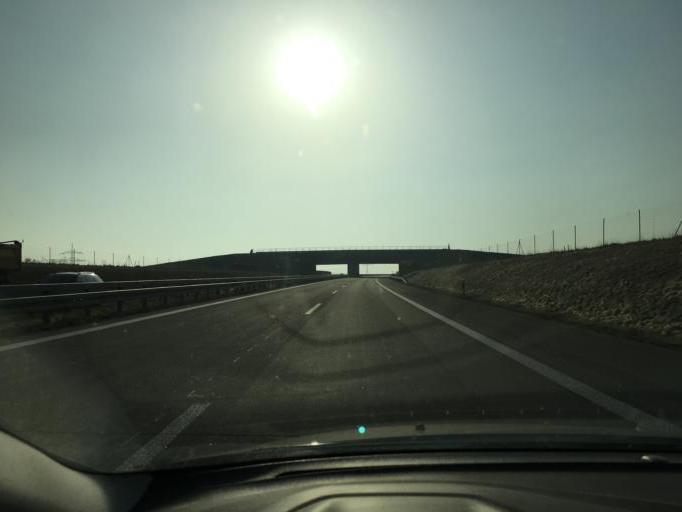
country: DE
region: Saxony
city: Frohburg
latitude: 51.0765
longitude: 12.5932
